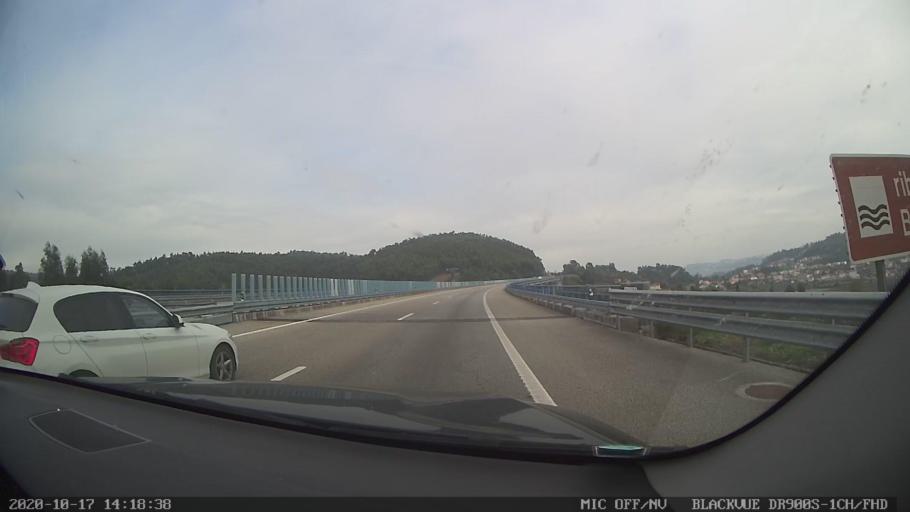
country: PT
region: Porto
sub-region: Lousada
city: Lousada
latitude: 41.3112
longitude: -8.2552
